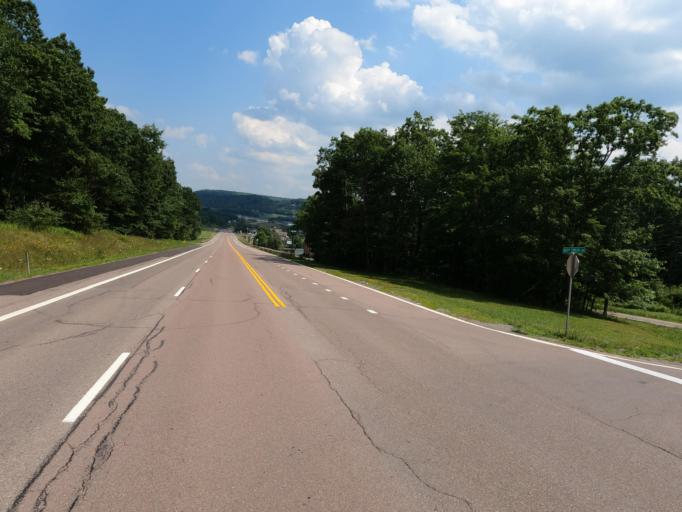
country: US
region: Maryland
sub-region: Garrett County
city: Oakland
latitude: 39.5650
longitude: -79.3647
